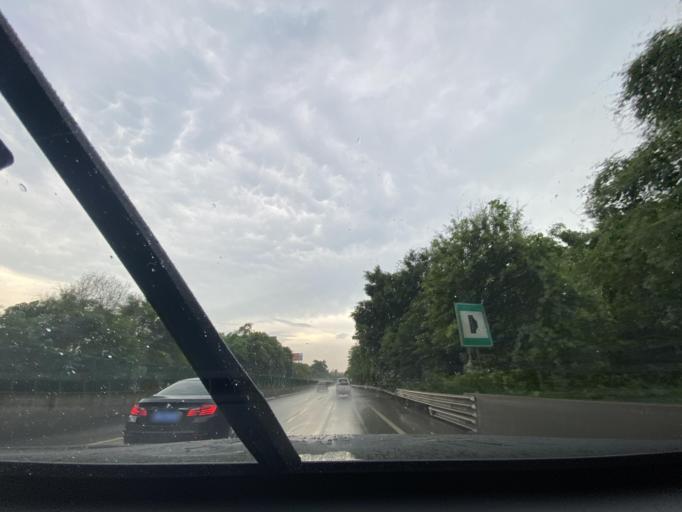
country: CN
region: Sichuan
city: Chonglong
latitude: 29.7630
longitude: 104.8156
